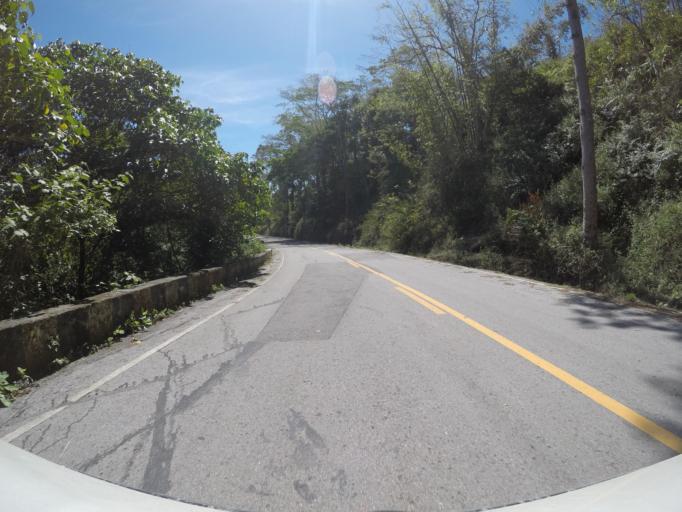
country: TL
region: Manufahi
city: Same
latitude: -8.8973
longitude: 125.9812
